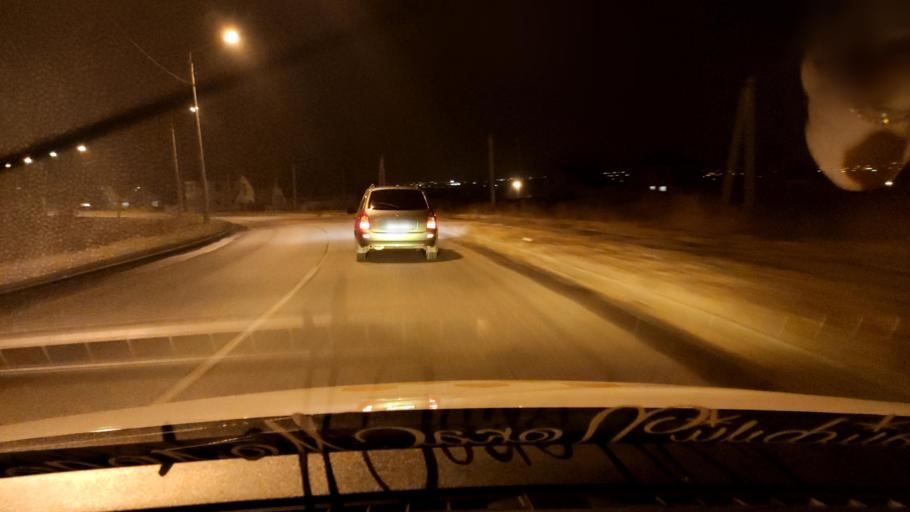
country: RU
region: Voronezj
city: Semiluki
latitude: 51.6624
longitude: 39.0400
